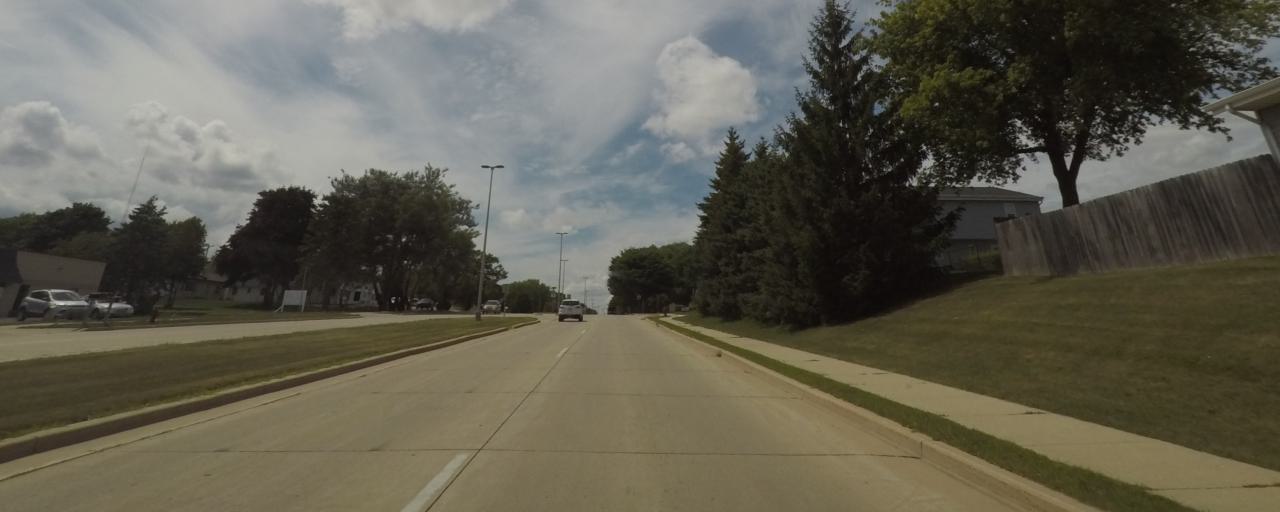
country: US
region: Wisconsin
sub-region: Milwaukee County
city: Hales Corners
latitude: 42.9592
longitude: -88.0507
